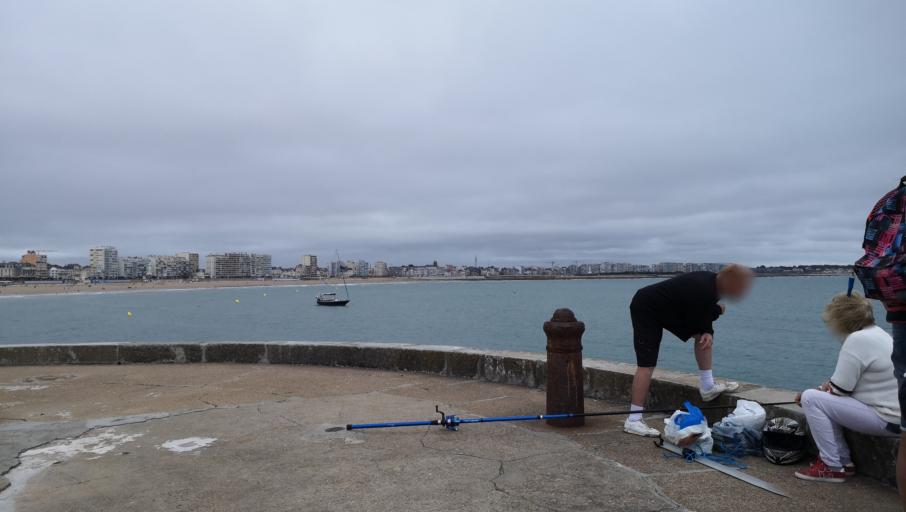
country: FR
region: Pays de la Loire
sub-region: Departement de la Vendee
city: Les Sables-d'Olonne
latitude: 46.4908
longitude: -1.7923
